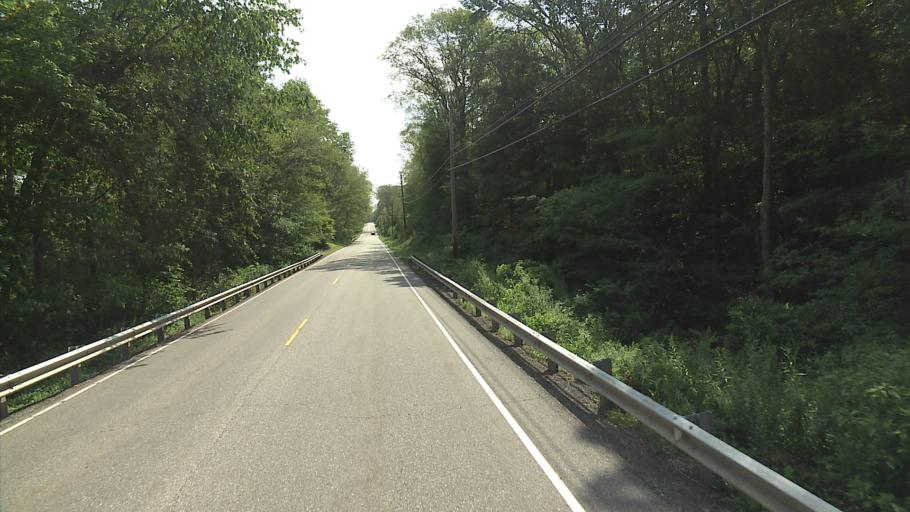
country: US
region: Connecticut
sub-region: New London County
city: Preston City
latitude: 41.5312
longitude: -71.9630
